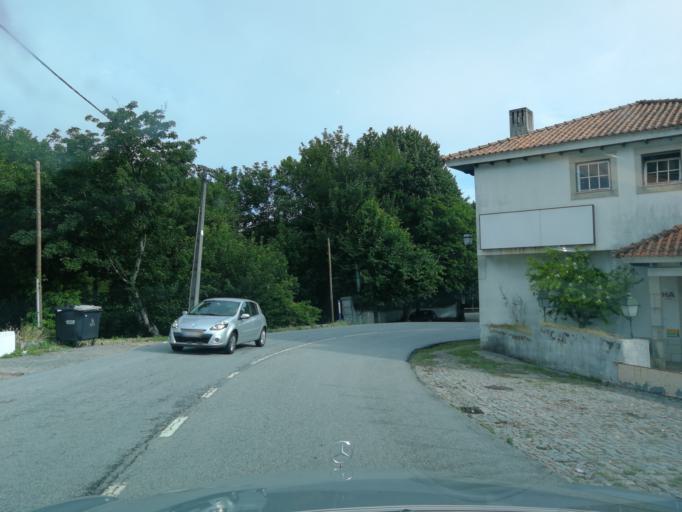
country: PT
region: Braga
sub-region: Braga
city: Adaufe
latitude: 41.5517
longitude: -8.3755
